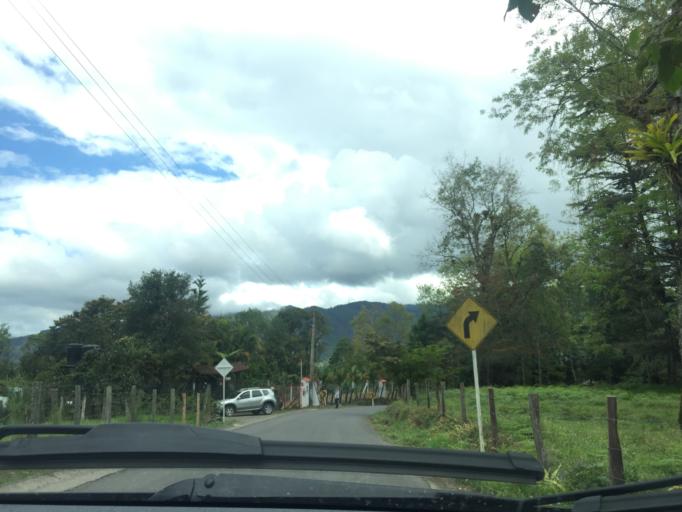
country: CO
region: Cundinamarca
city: Supata
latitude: 5.0540
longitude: -74.2393
